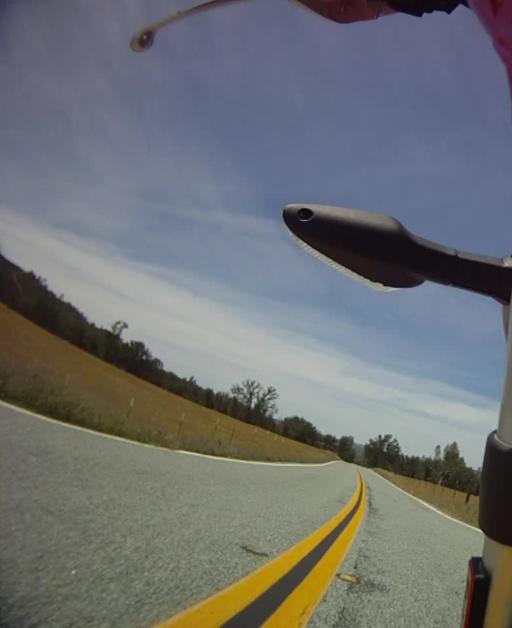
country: US
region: California
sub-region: Santa Clara County
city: Morgan Hill
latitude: 37.3532
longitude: -121.4784
